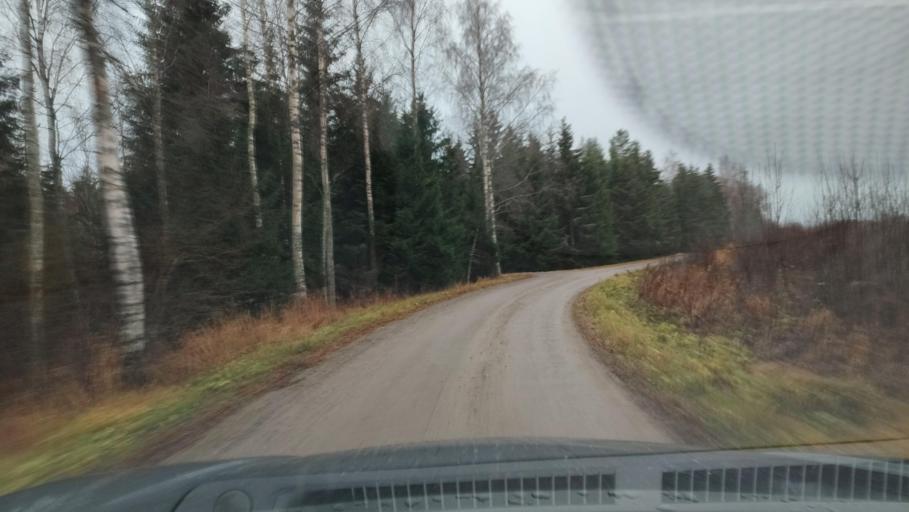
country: FI
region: Ostrobothnia
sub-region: Sydosterbotten
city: Kristinestad
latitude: 62.2397
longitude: 21.4699
